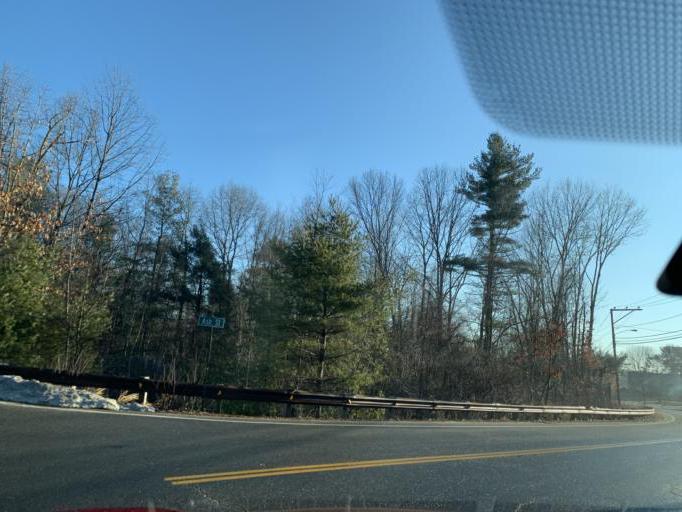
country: US
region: New Hampshire
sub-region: Rockingham County
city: Derry
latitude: 42.8842
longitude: -71.3361
